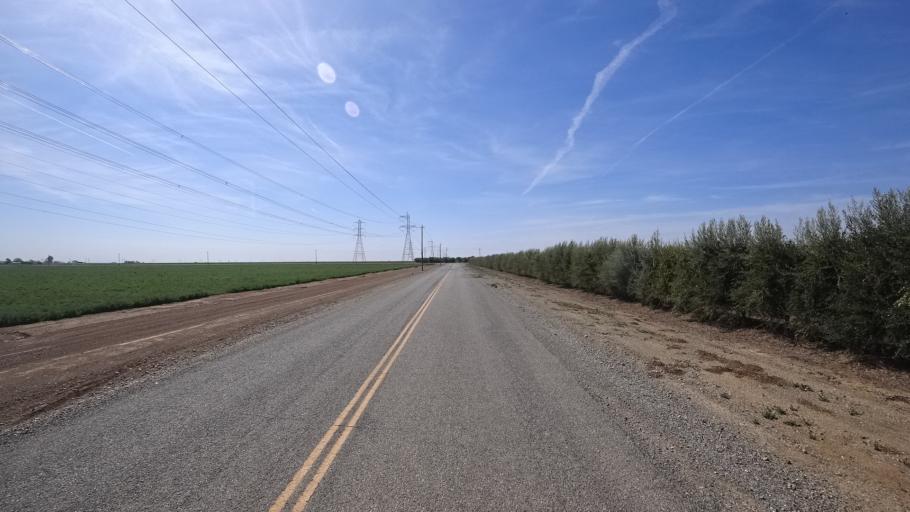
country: US
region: California
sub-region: Glenn County
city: Willows
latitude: 39.5265
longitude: -122.2869
